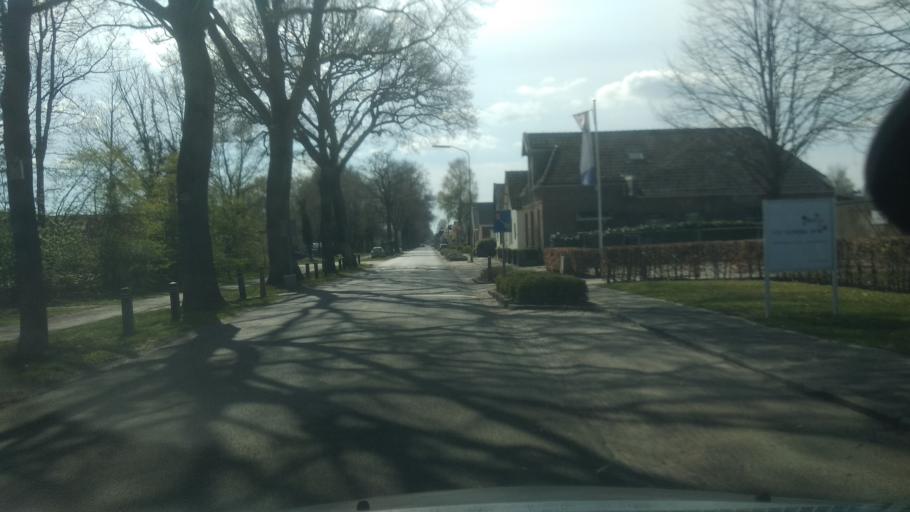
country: NL
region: Groningen
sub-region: Gemeente Stadskanaal
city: Stadskanaal
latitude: 52.9435
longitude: 6.9025
